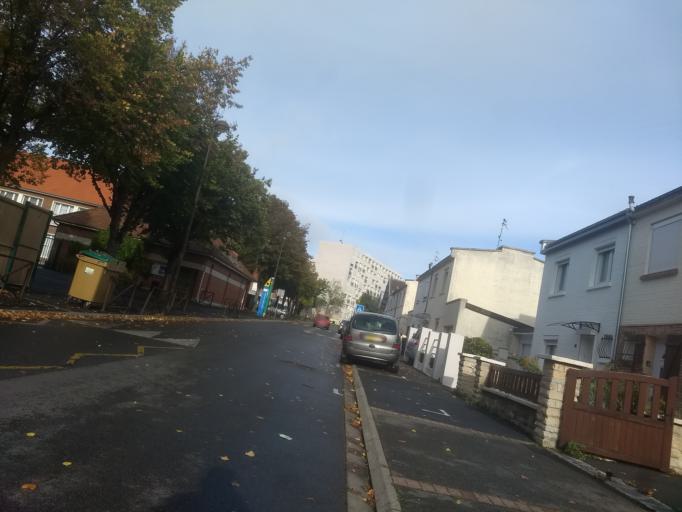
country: FR
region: Nord-Pas-de-Calais
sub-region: Departement du Pas-de-Calais
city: Achicourt
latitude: 50.2892
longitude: 2.7515
